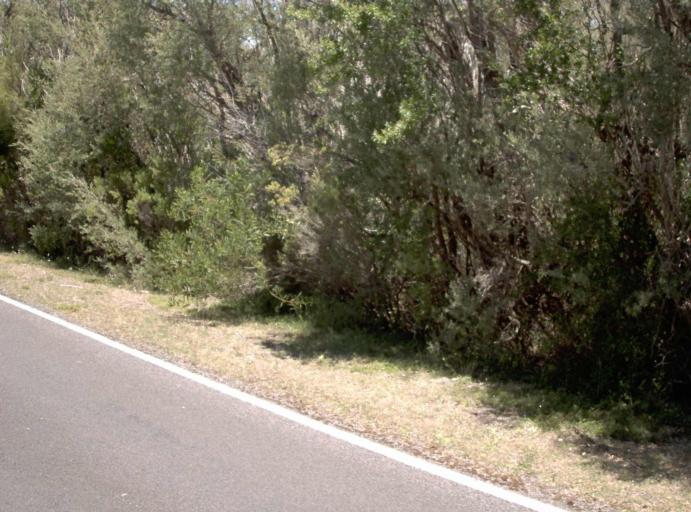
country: AU
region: Victoria
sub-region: Latrobe
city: Morwell
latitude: -38.8615
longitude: 146.2538
